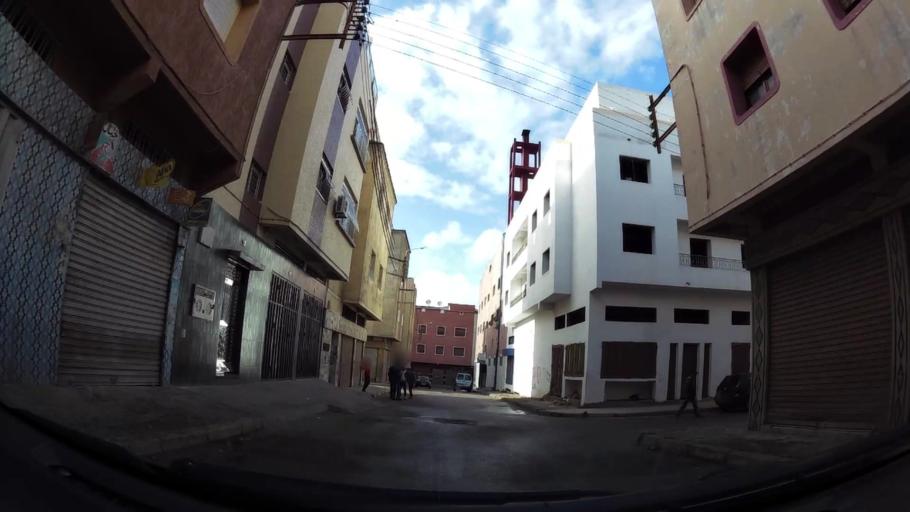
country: MA
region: Grand Casablanca
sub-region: Casablanca
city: Casablanca
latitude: 33.5438
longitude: -7.5935
